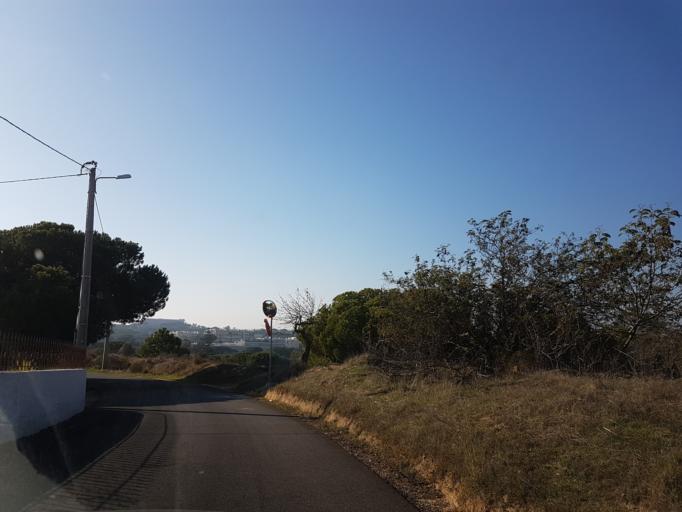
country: PT
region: Faro
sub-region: Albufeira
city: Ferreiras
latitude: 37.0964
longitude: -8.1971
